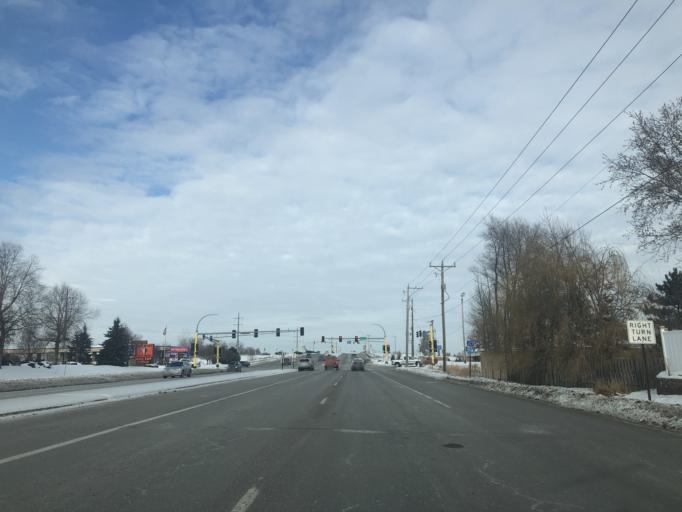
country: US
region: Minnesota
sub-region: Anoka County
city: Lexington
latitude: 45.1557
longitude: -93.1632
